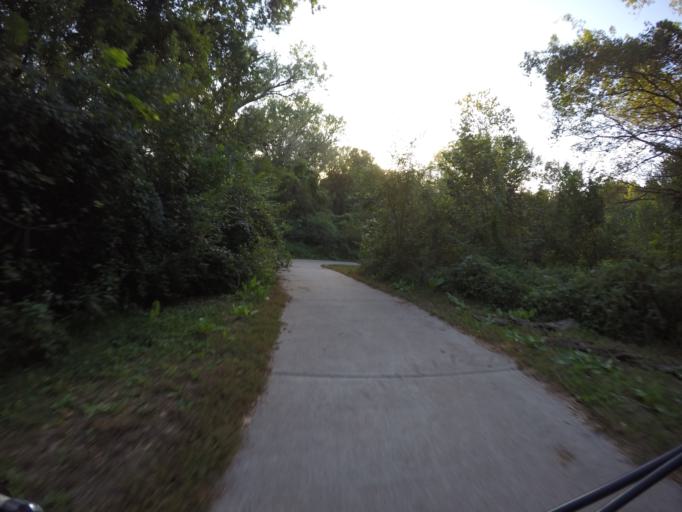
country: US
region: Kansas
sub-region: Riley County
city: Manhattan
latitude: 39.1711
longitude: -96.5980
